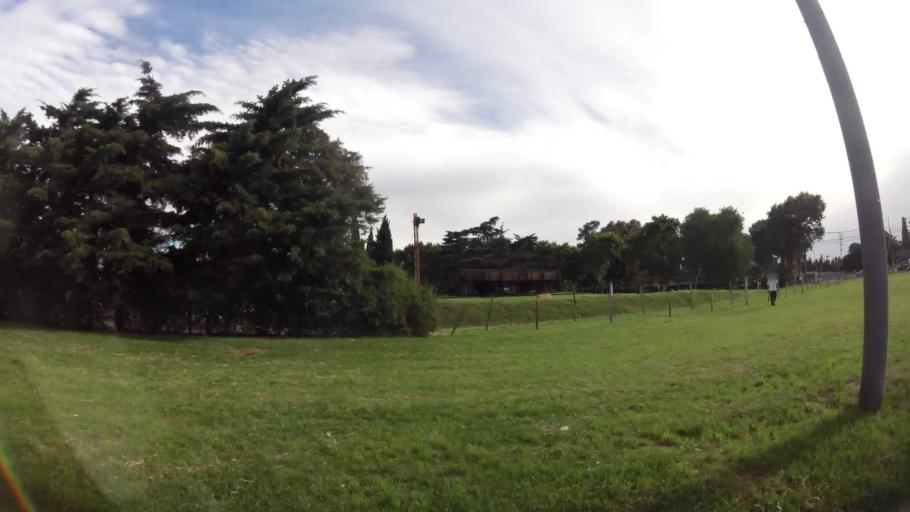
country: AR
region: Santa Fe
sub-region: Departamento de Rosario
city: Rosario
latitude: -32.9308
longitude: -60.6720
